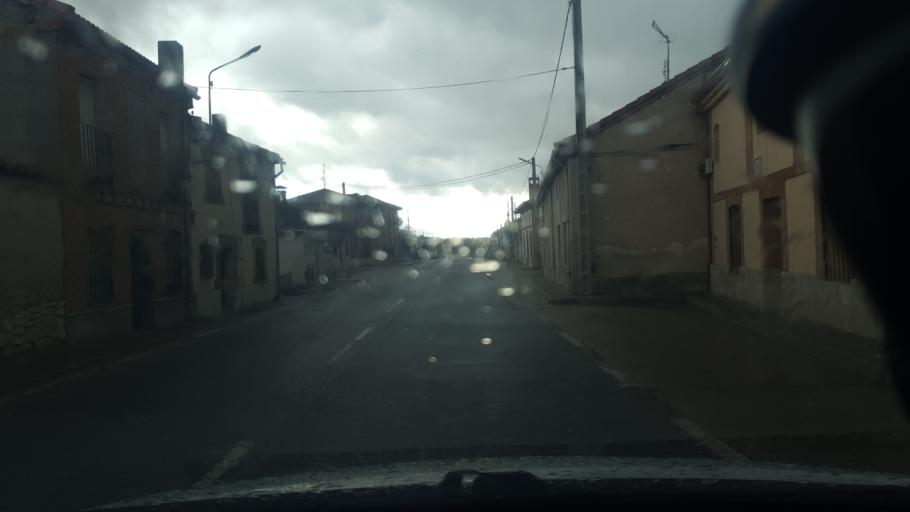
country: ES
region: Castille and Leon
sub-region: Provincia de Segovia
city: Samboal
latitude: 41.2993
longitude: -4.4074
